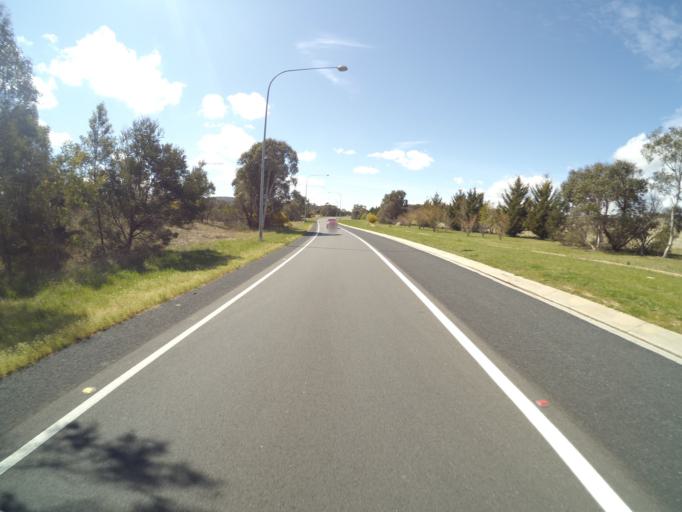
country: AU
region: New South Wales
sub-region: Goulburn Mulwaree
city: Goulburn
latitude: -34.7417
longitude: 149.7746
